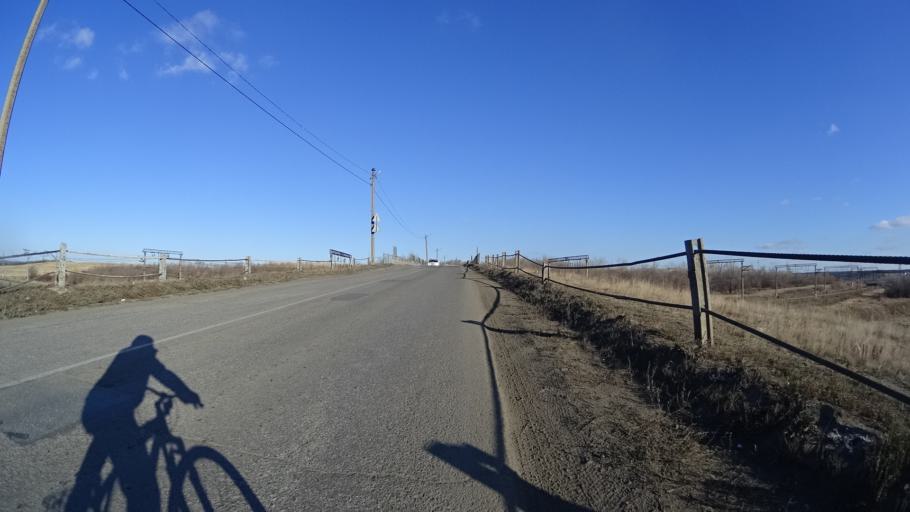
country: RU
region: Chelyabinsk
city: Troitsk
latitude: 54.0798
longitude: 61.6008
